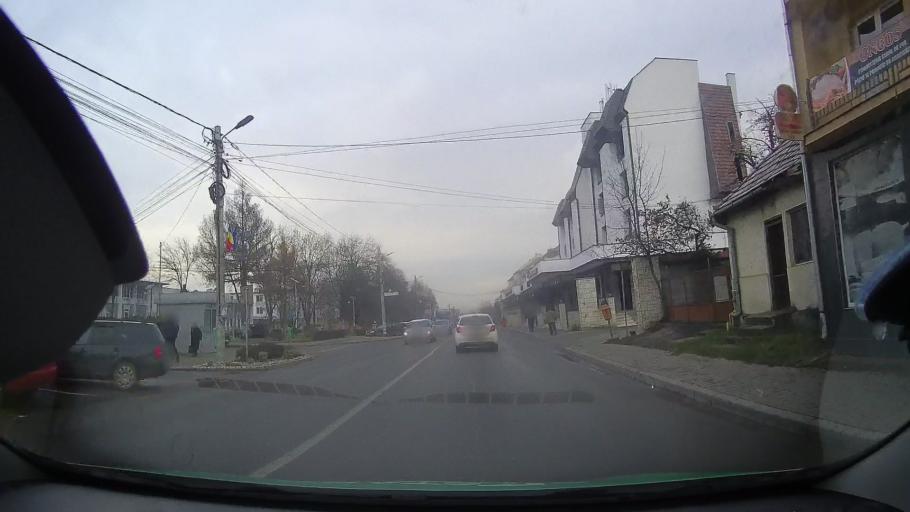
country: RO
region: Mures
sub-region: Comuna Ludus
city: Ludus
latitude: 46.4735
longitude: 24.0954
